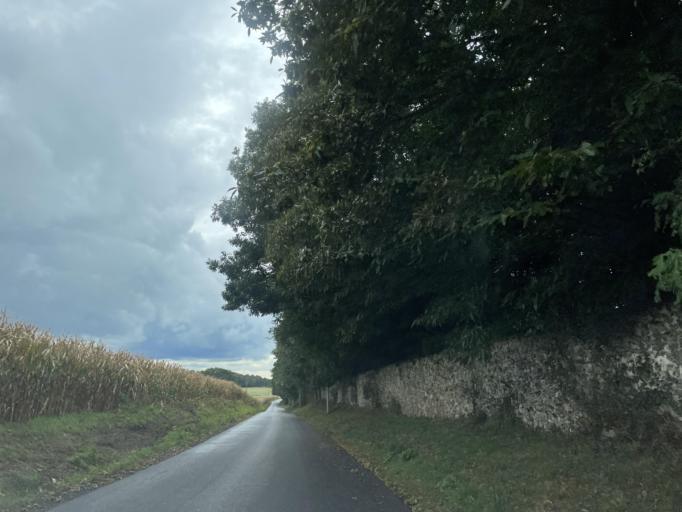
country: FR
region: Ile-de-France
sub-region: Departement de Seine-et-Marne
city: Trilport
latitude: 48.9375
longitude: 2.9817
